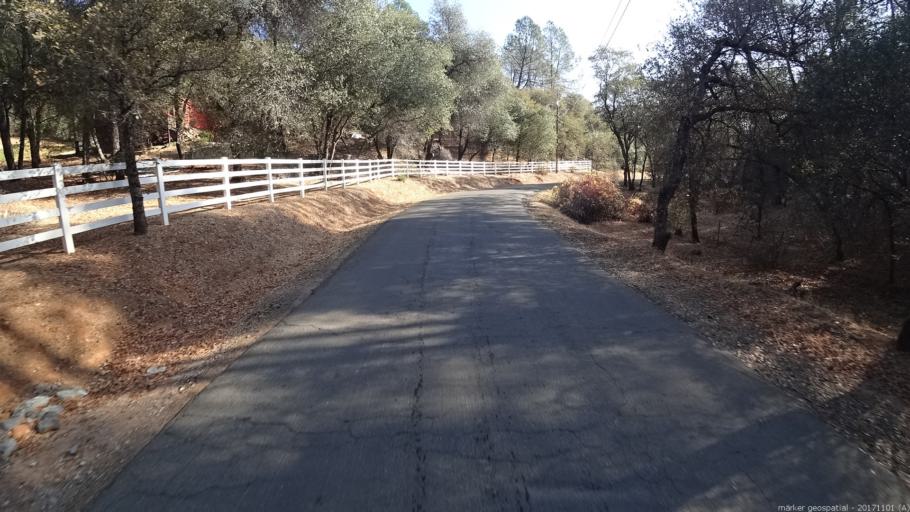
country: US
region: California
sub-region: Shasta County
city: Shasta Lake
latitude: 40.7088
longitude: -122.3243
